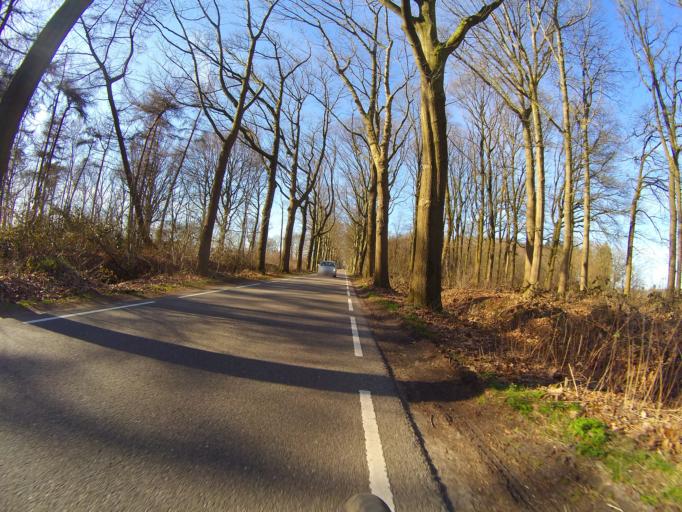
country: NL
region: Utrecht
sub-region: Gemeente Leusden
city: Leusden
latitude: 52.1023
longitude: 5.4638
